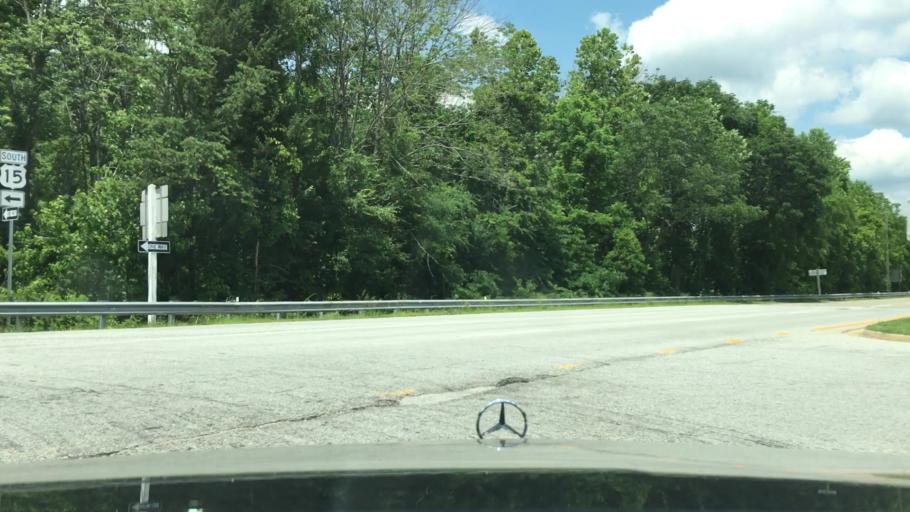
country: US
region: Virginia
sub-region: Prince Edward County
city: Farmville
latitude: 37.2704
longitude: -78.4044
